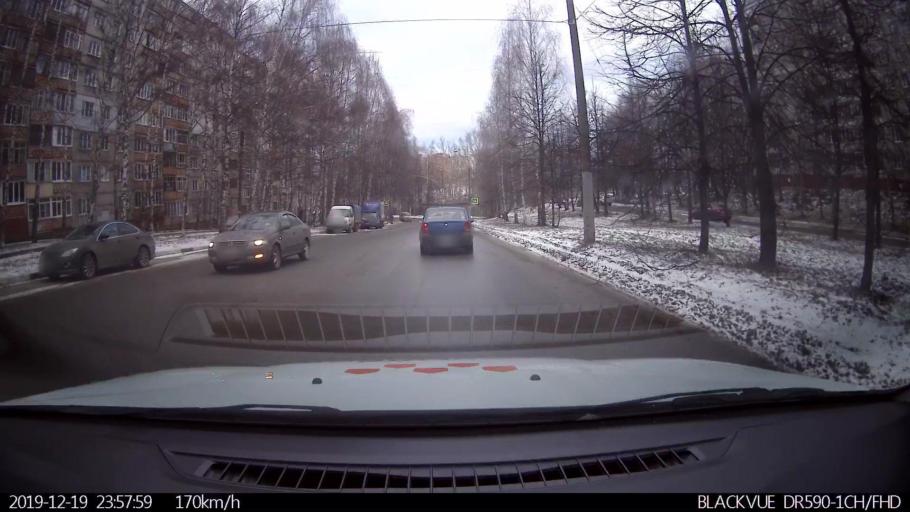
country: RU
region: Jaroslavl
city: Kukoboy
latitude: 58.8695
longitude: 39.6345
